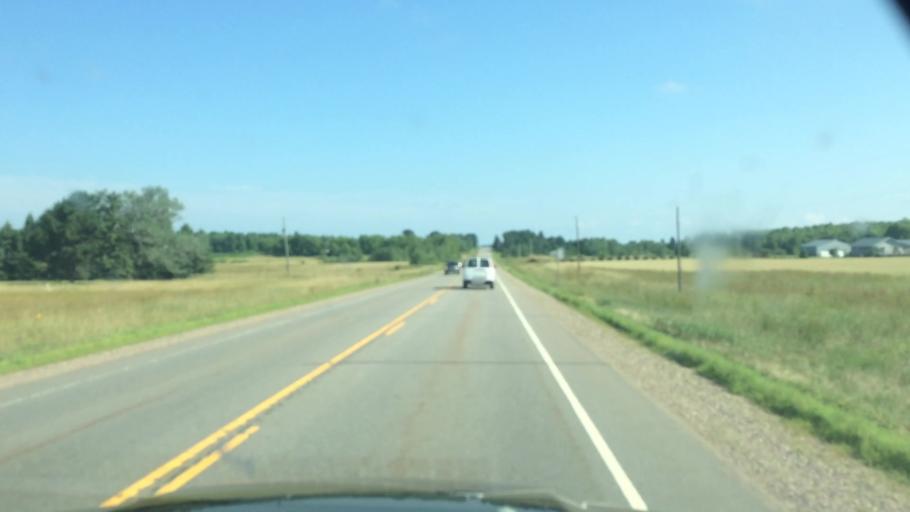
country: US
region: Wisconsin
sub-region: Lincoln County
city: Merrill
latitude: 45.1557
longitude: -89.4667
